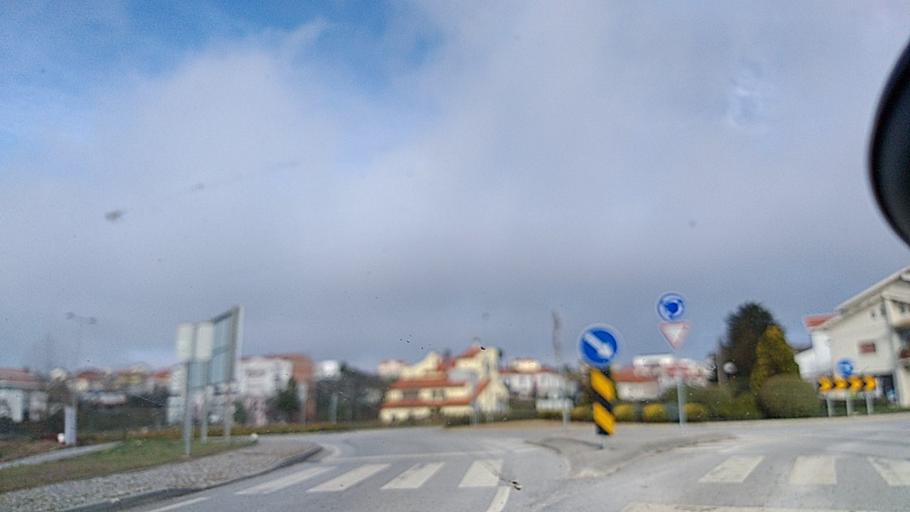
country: PT
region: Guarda
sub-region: Aguiar da Beira
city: Aguiar da Beira
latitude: 40.8176
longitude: -7.5380
